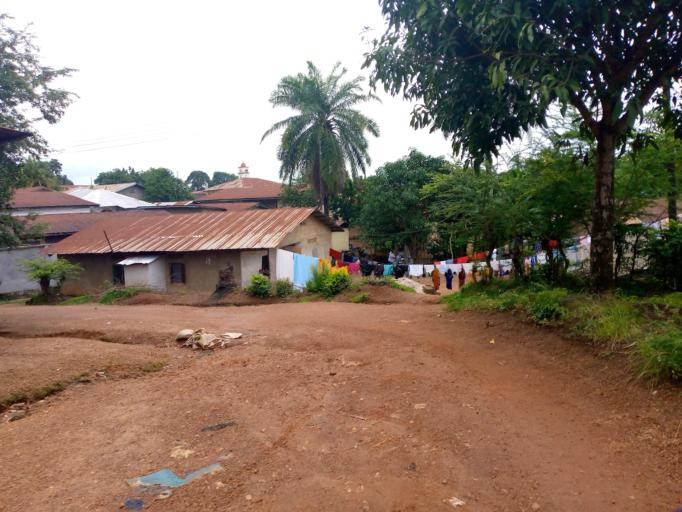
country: SL
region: Eastern Province
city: Kenema
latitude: 7.8713
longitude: -11.1806
